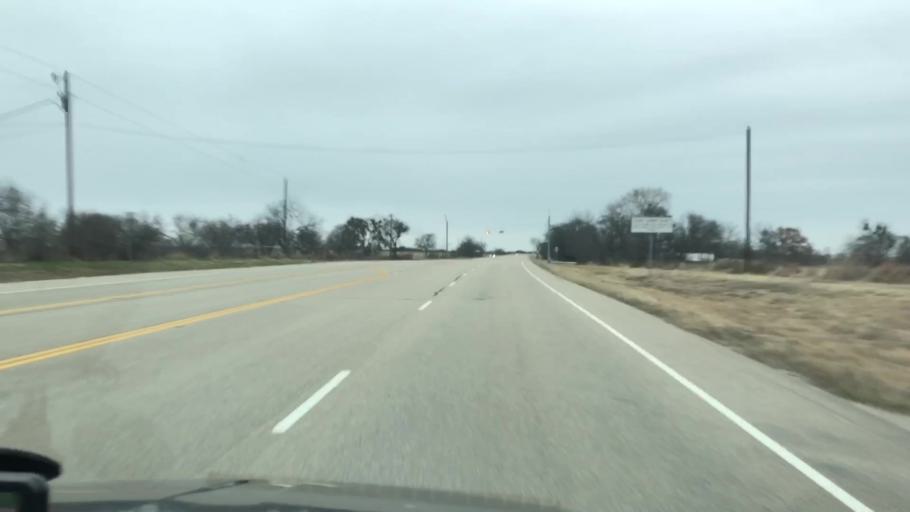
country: US
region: Texas
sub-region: Hamilton County
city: Hico
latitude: 31.8734
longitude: -98.1082
